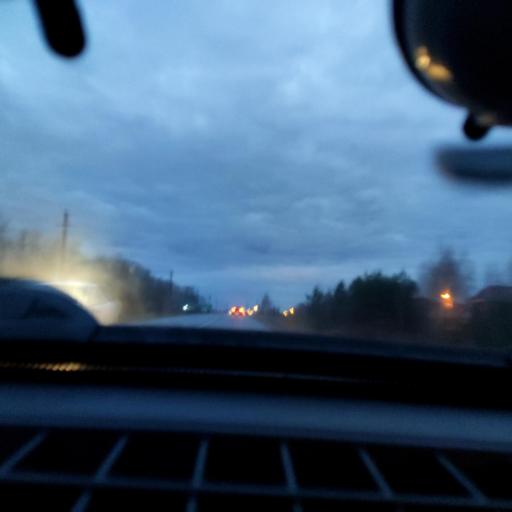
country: RU
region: Bashkortostan
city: Iglino
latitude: 54.7936
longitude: 56.2740
